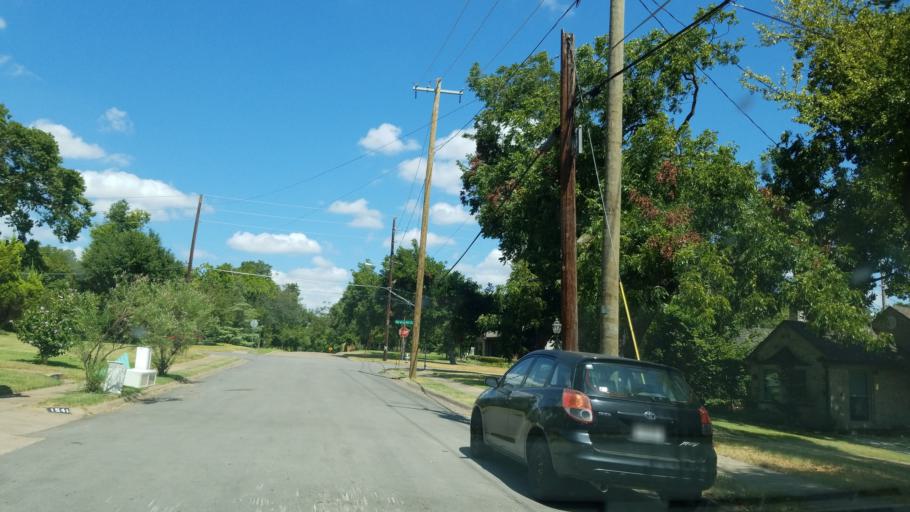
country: US
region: Texas
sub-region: Dallas County
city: Dallas
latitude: 32.7636
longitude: -96.8315
